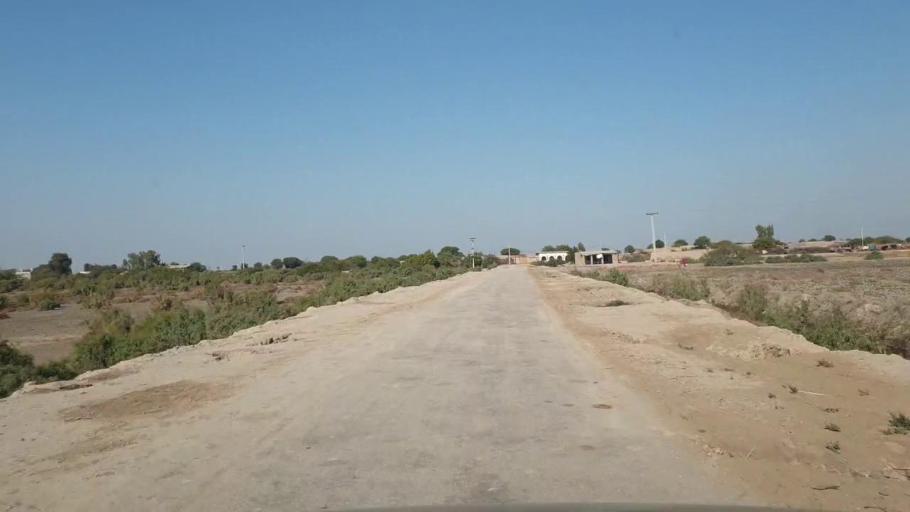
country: PK
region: Sindh
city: Shahpur Chakar
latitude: 26.1560
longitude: 68.6762
